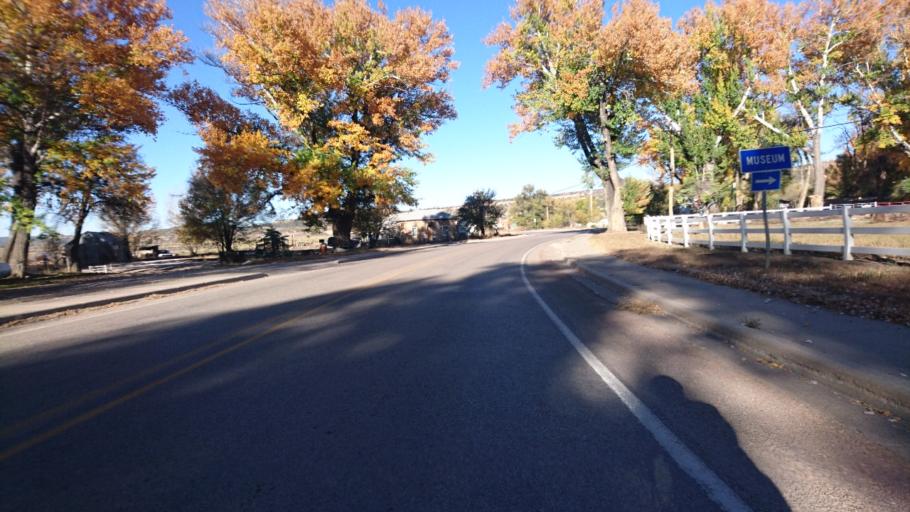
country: US
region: New Mexico
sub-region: McKinley County
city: Black Rock
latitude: 35.1328
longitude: -108.4955
